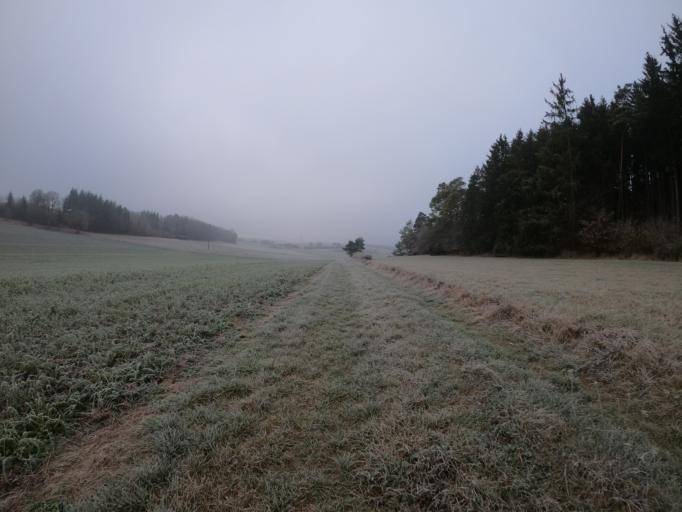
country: DE
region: Baden-Wuerttemberg
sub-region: Tuebingen Region
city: Westerstetten
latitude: 48.4987
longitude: 9.9535
